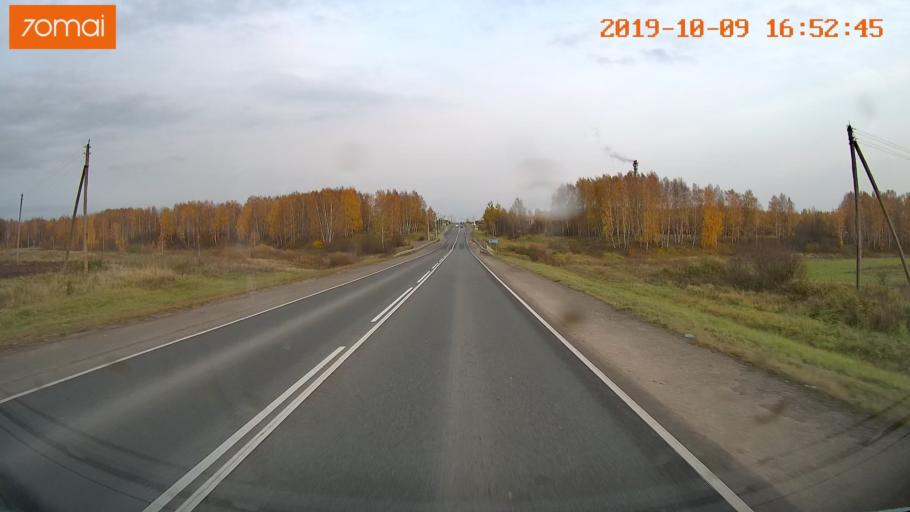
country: RU
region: Ivanovo
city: Privolzhsk
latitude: 57.3792
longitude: 41.2550
